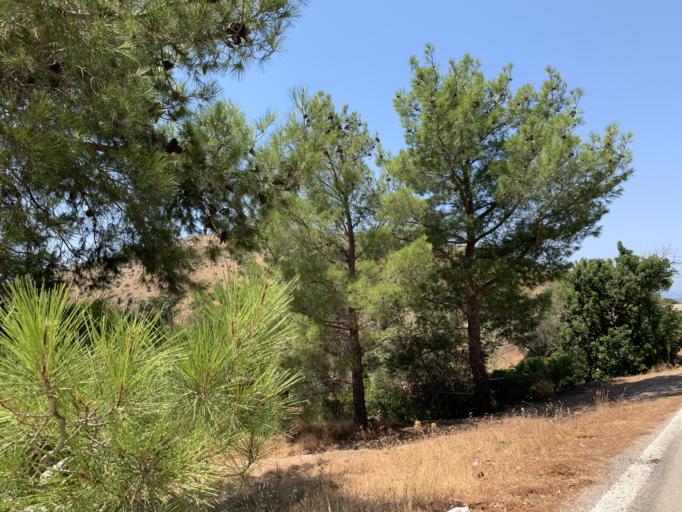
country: GR
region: North Aegean
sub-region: Chios
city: Vrontados
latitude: 38.4366
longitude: 25.9760
